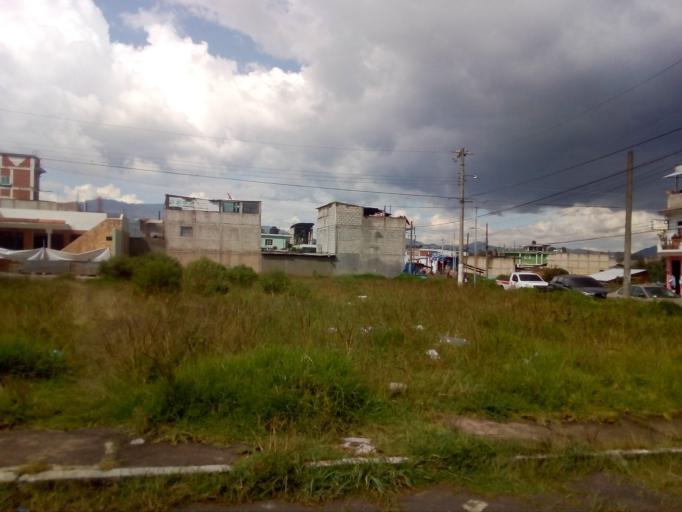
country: GT
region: Quetzaltenango
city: Quetzaltenango
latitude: 14.8534
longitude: -91.5082
